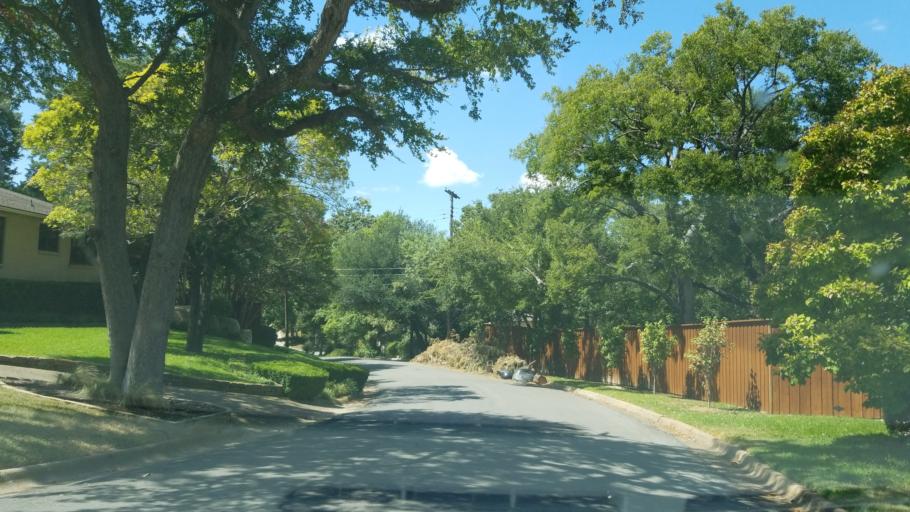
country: US
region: Texas
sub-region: Dallas County
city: Dallas
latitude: 32.7648
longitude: -96.8328
